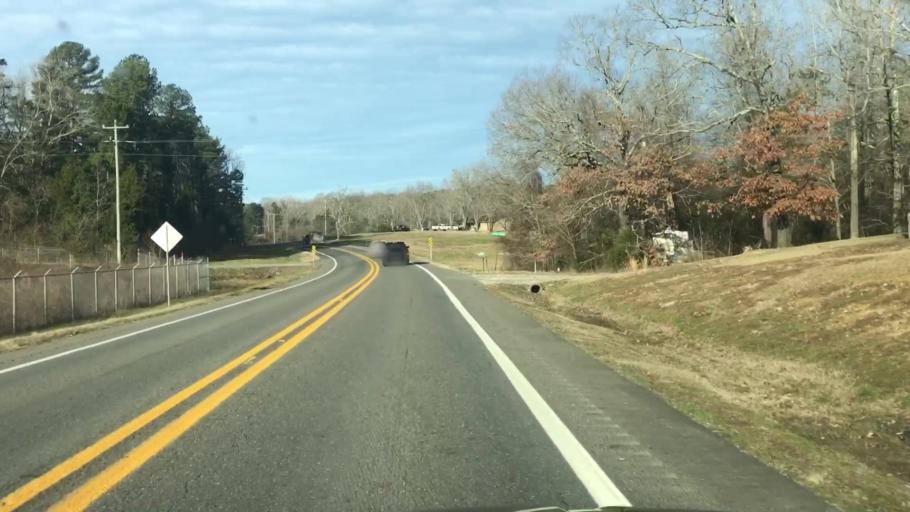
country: US
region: Arkansas
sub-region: Montgomery County
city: Mount Ida
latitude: 34.5314
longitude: -93.5320
